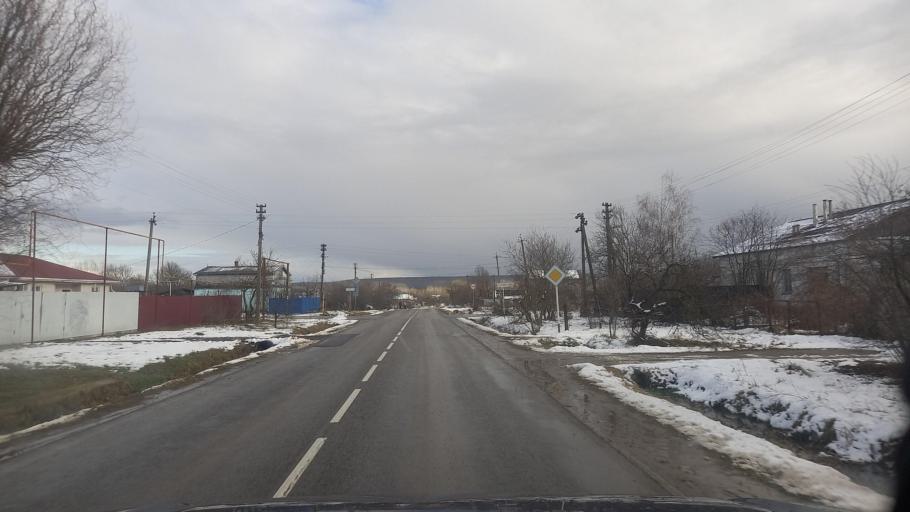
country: RU
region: Krasnodarskiy
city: Smolenskaya
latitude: 44.7765
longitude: 38.8423
